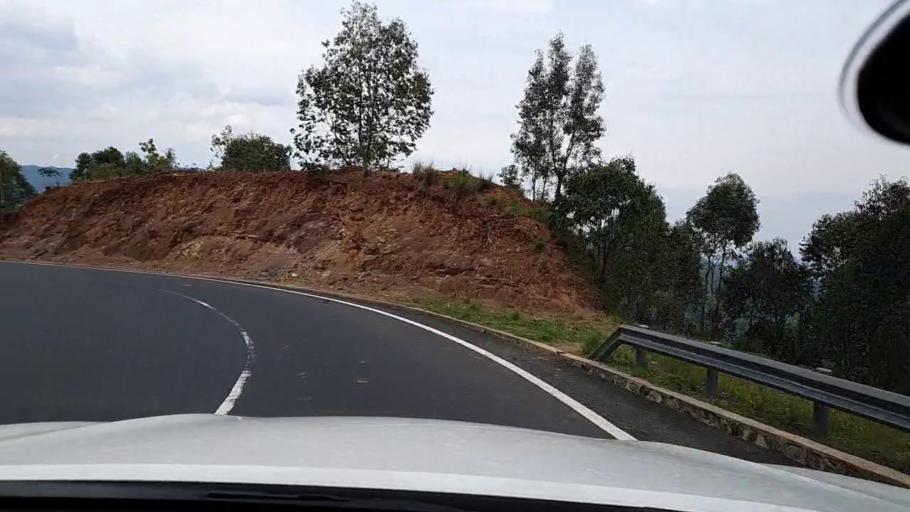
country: RW
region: Western Province
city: Kibuye
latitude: -2.1806
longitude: 29.2888
